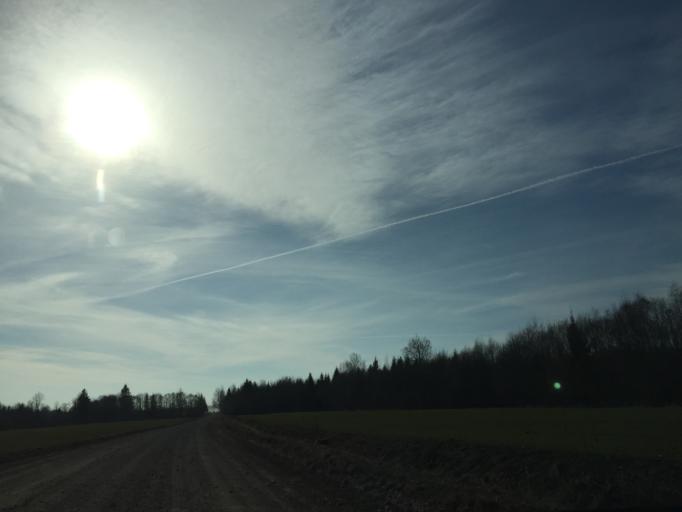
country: LV
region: Saulkrastu
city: Saulkrasti
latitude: 57.2989
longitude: 24.5481
